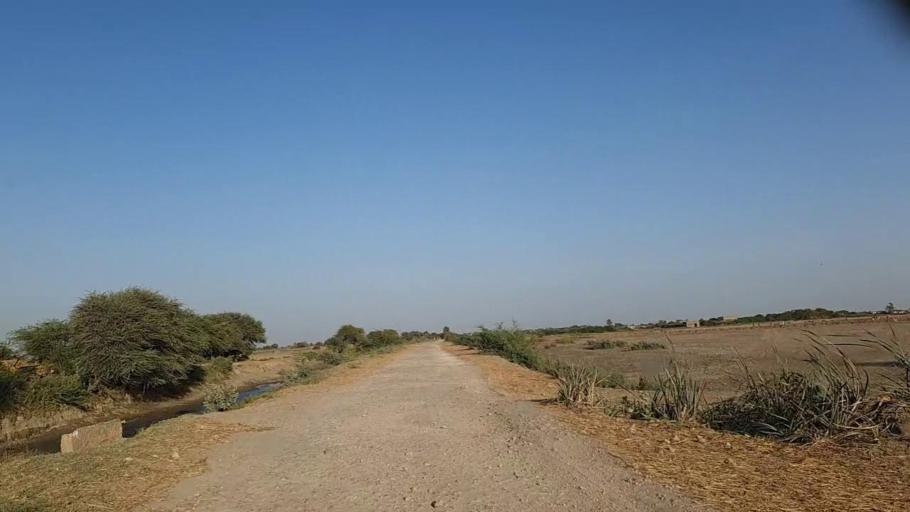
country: PK
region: Sindh
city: Jati
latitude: 24.4154
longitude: 68.3073
